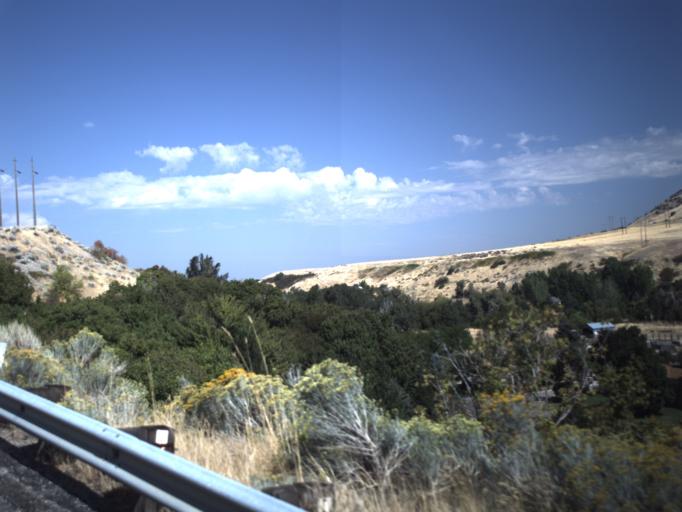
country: US
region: Utah
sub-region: Cache County
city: Hyrum
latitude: 41.6319
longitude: -111.8117
